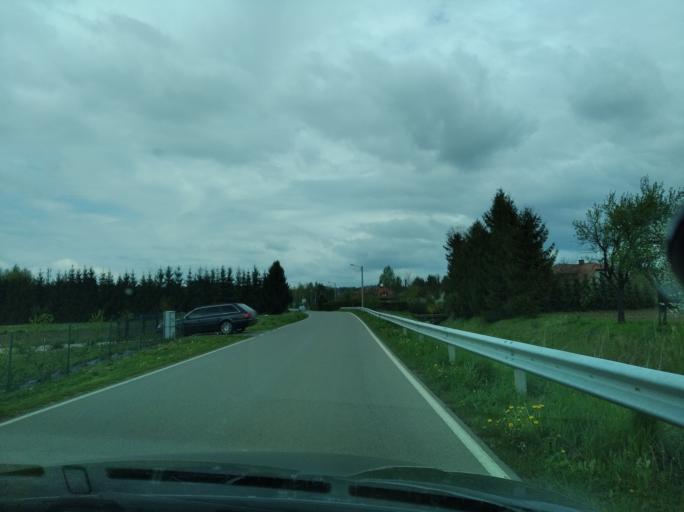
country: PL
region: Subcarpathian Voivodeship
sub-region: Powiat brzozowski
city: Turze Pole
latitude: 49.6556
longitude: 21.9954
